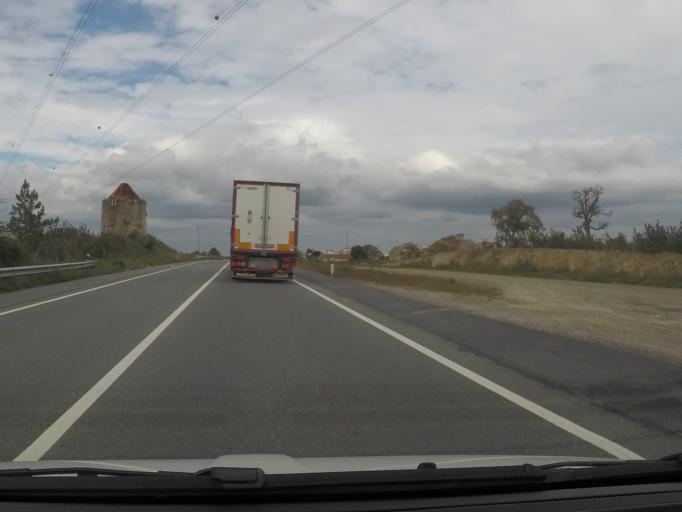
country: PT
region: Setubal
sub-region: Santiago do Cacem
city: Santiago do Cacem
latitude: 38.0720
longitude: -8.6536
